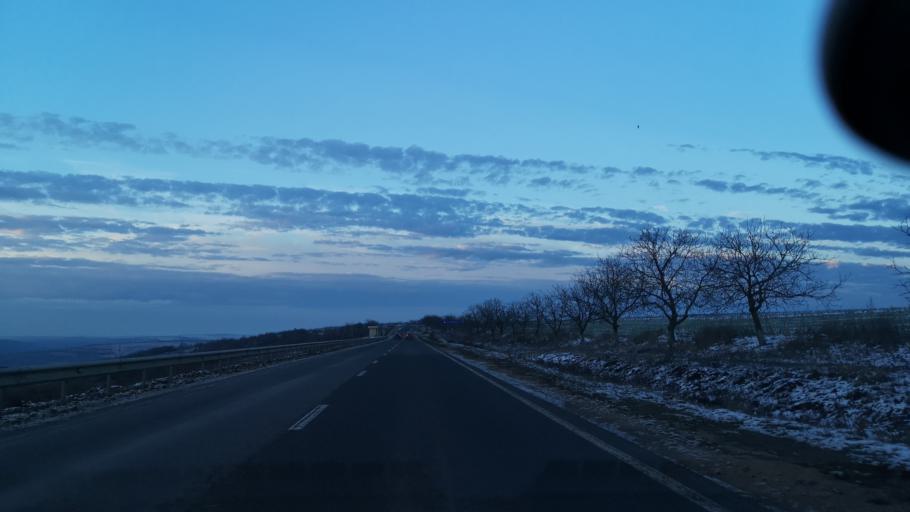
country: MD
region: Rezina
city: Saharna
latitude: 47.6028
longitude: 28.8318
